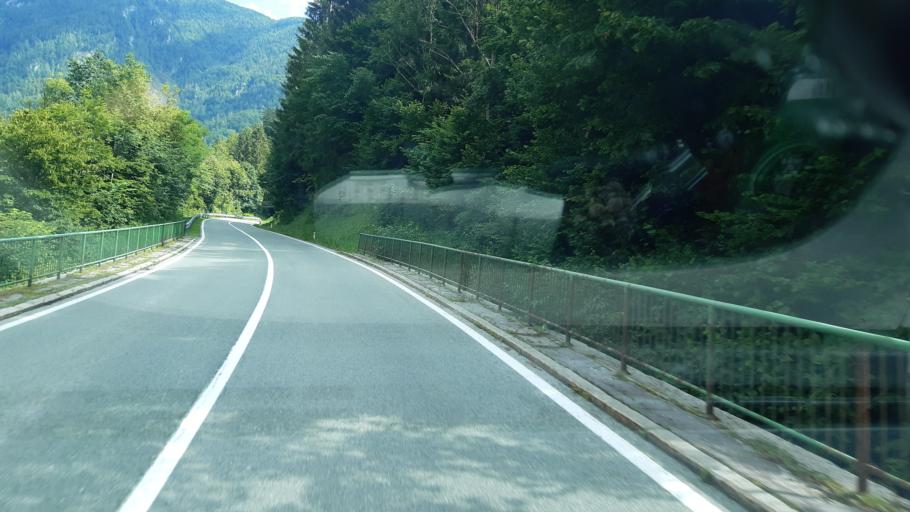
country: SI
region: Trzic
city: Trzic
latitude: 46.3712
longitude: 14.3029
